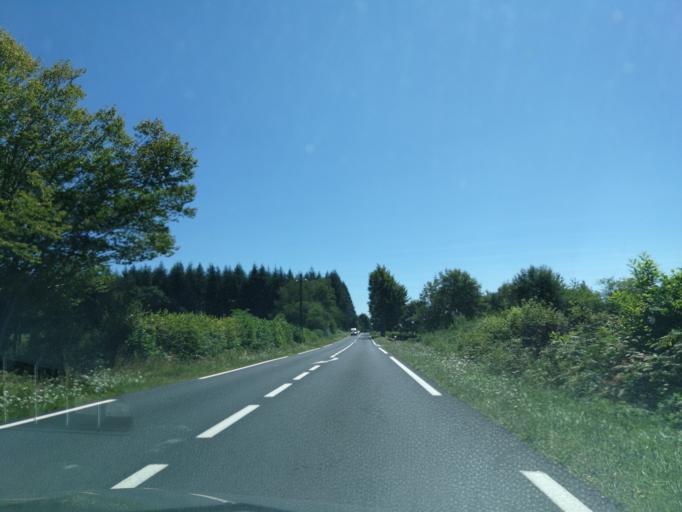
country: FR
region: Limousin
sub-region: Departement de la Correze
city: Saint-Privat
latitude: 45.0029
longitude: 2.0522
